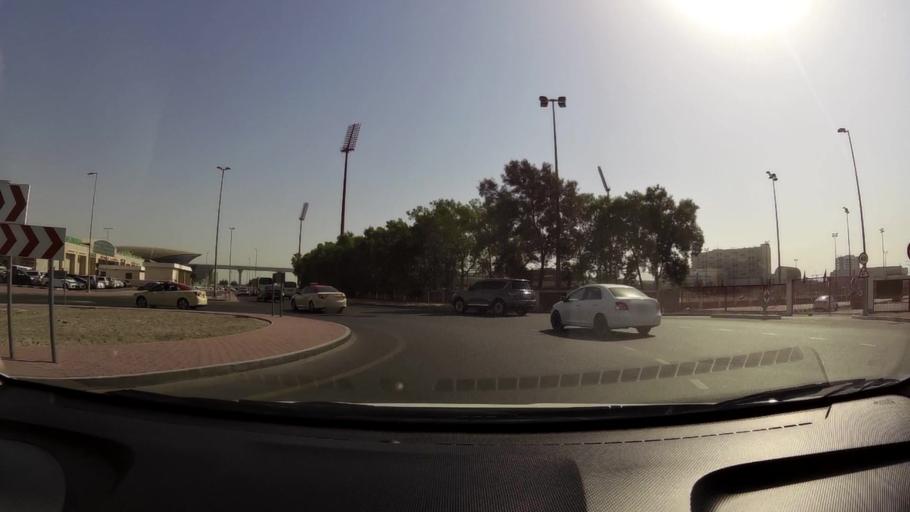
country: AE
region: Ash Shariqah
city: Sharjah
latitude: 25.2810
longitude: 55.3622
